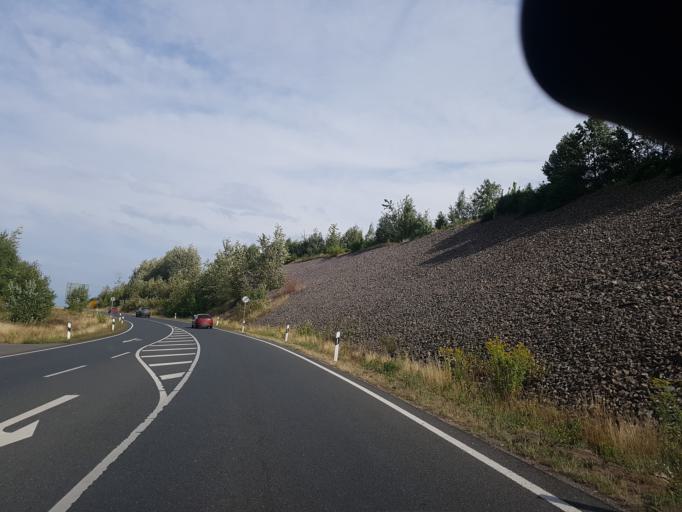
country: DE
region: Saxony
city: Dobeln
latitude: 51.1238
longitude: 13.0695
